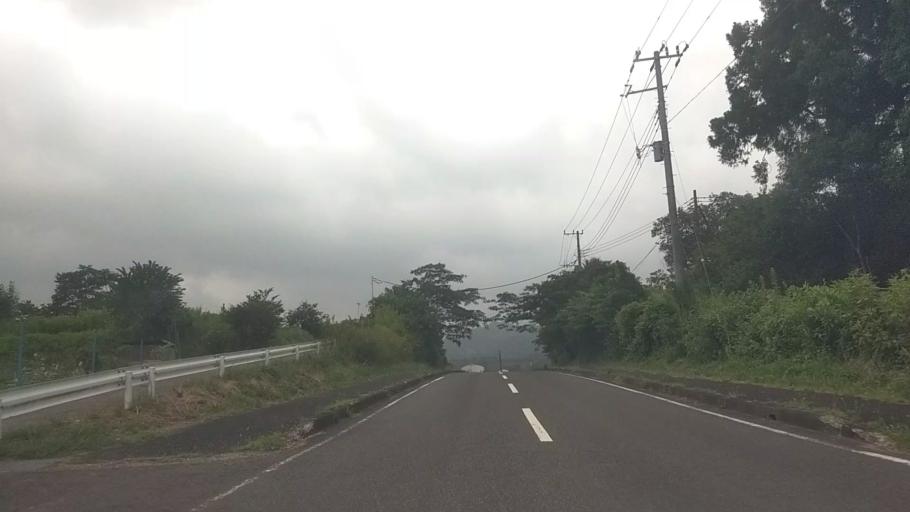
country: JP
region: Chiba
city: Kawaguchi
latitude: 35.2346
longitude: 140.0859
